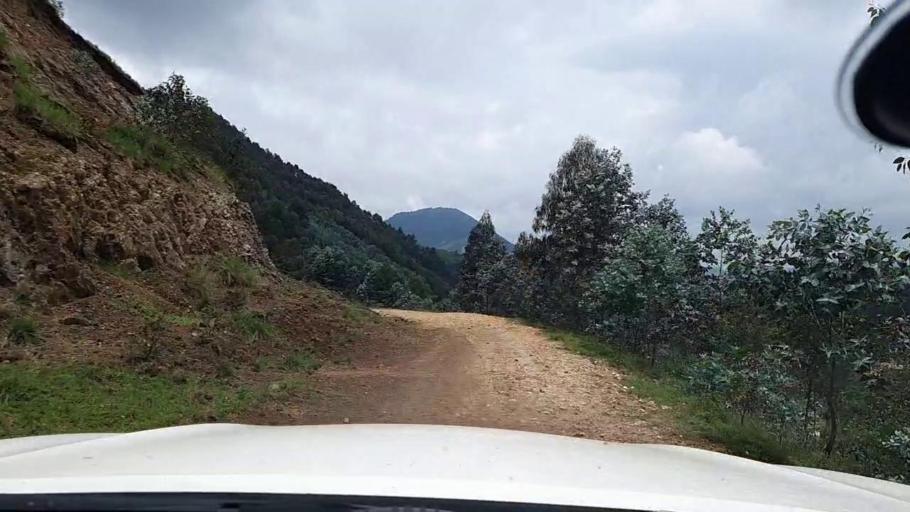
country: RW
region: Western Province
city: Kibuye
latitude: -2.1524
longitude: 29.4528
